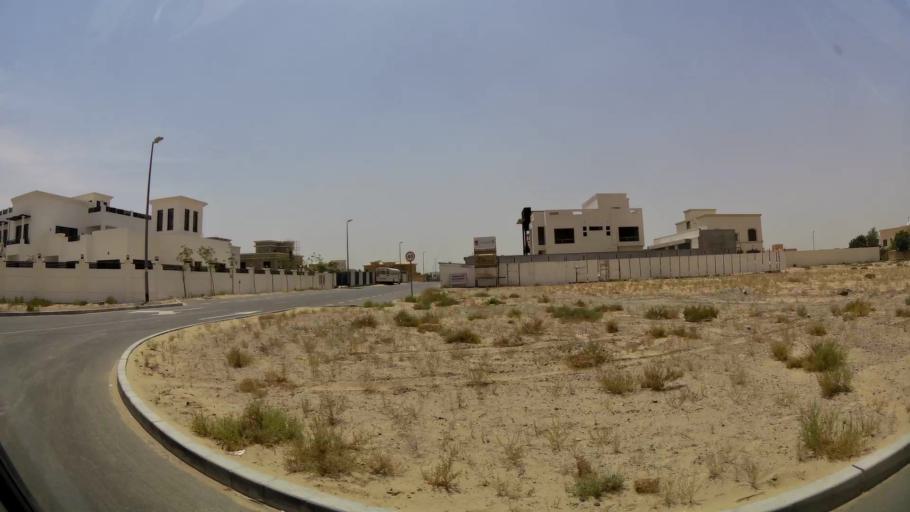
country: AE
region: Ash Shariqah
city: Sharjah
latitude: 25.2425
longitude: 55.5059
